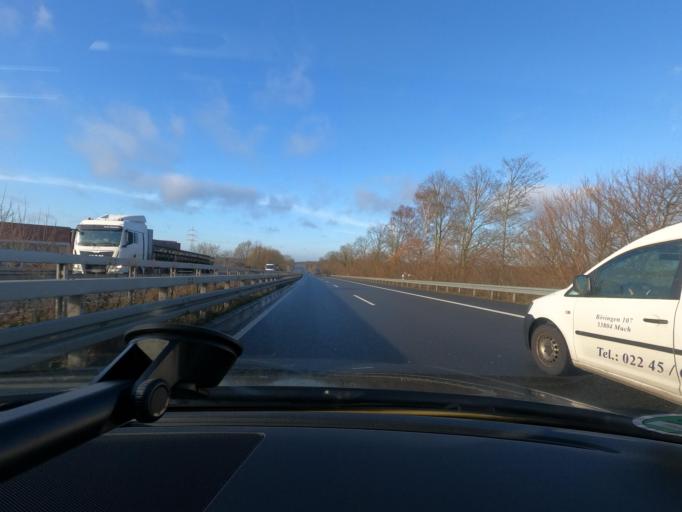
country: DE
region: North Rhine-Westphalia
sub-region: Regierungsbezirk Dusseldorf
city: Ratingen
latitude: 51.3490
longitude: 6.8394
